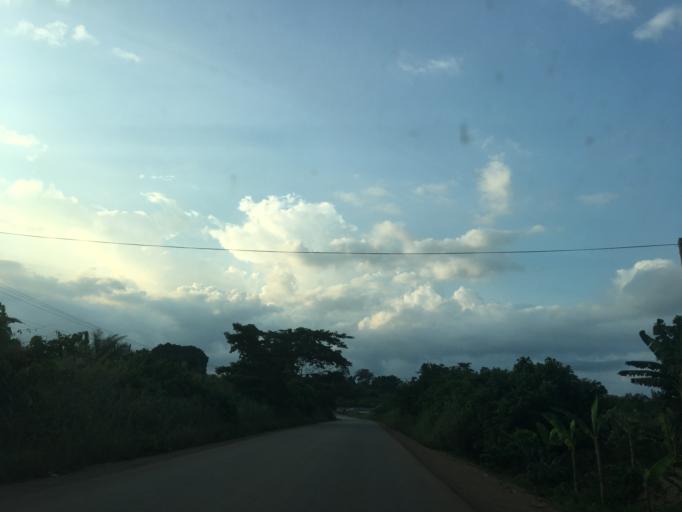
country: GH
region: Western
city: Bibiani
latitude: 6.6576
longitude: -2.4264
